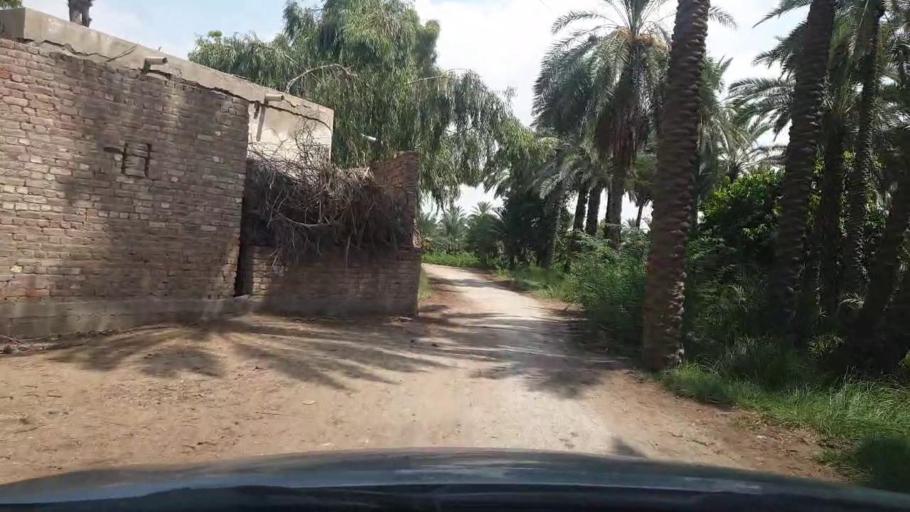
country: PK
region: Sindh
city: Kot Diji
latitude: 27.3935
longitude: 68.7436
